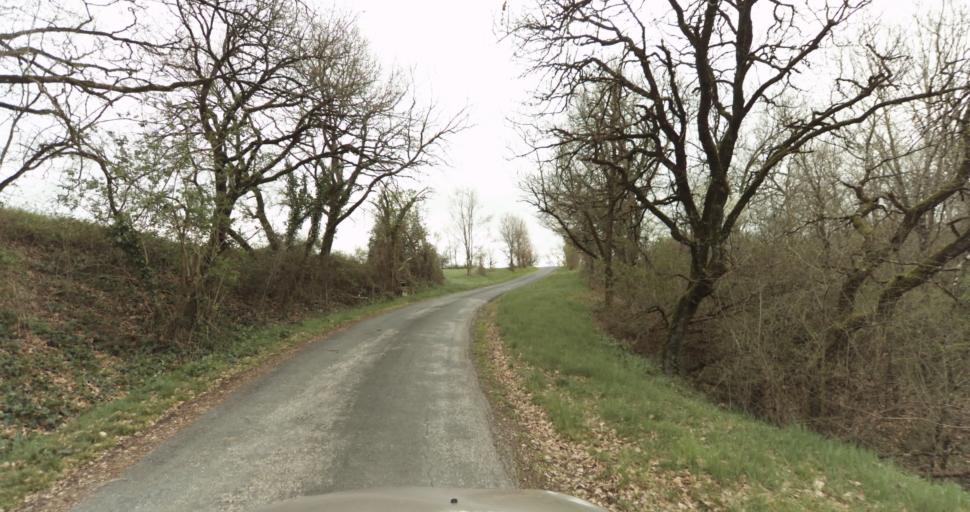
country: FR
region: Midi-Pyrenees
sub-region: Departement du Tarn
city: Puygouzon
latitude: 43.8660
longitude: 2.1813
